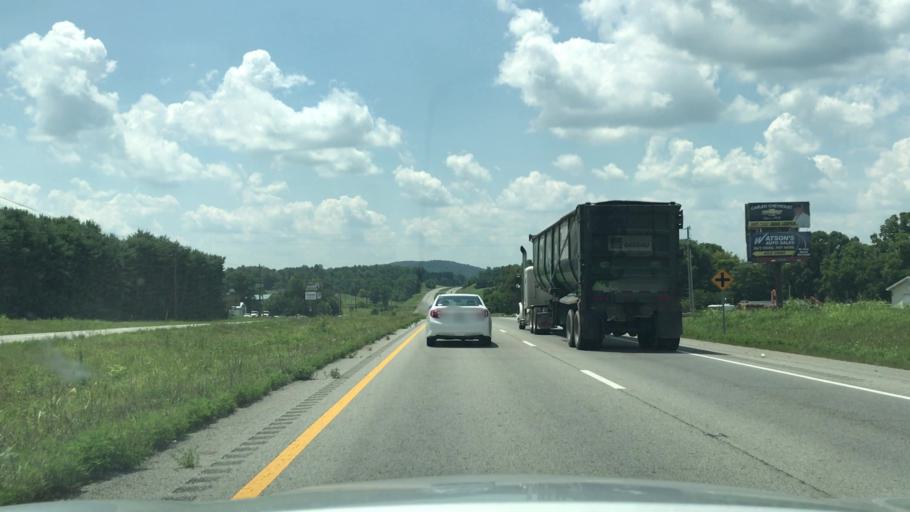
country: US
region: Tennessee
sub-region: Overton County
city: Livingston
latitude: 36.3543
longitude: -85.3437
